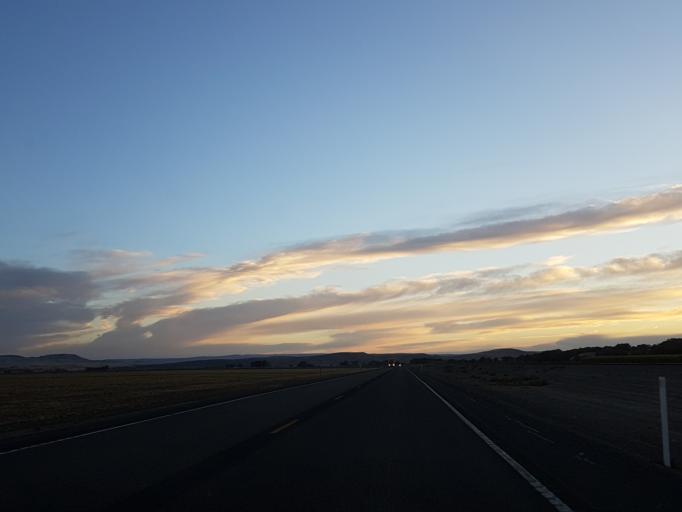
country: US
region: Oregon
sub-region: Malheur County
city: Vale
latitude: 43.9550
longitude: -117.2882
